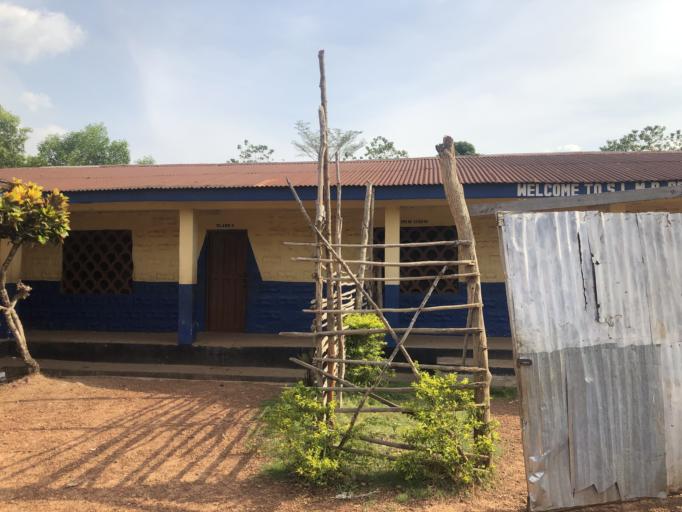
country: SL
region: Northern Province
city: Yonibana
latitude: 8.4385
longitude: -12.2415
